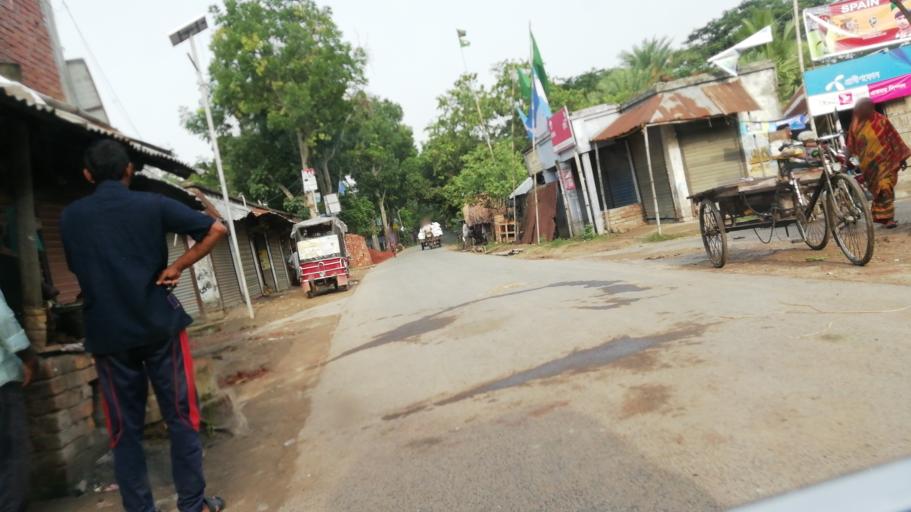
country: BD
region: Khulna
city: Bhatpara Abhaynagar
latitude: 23.0357
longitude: 89.2958
